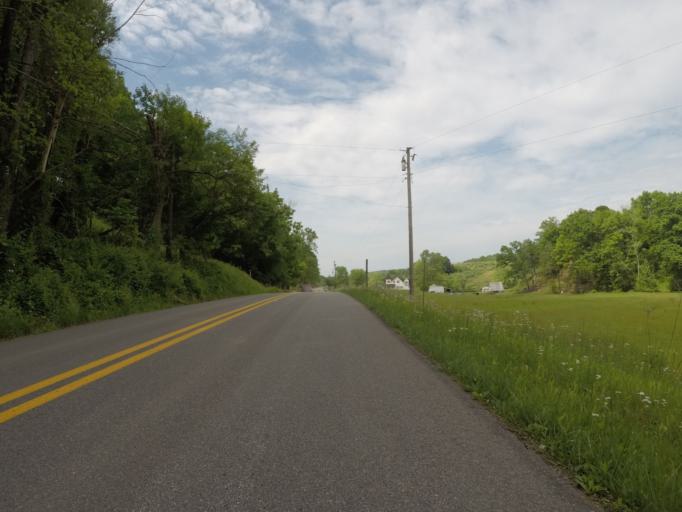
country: US
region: West Virginia
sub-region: Wayne County
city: Ceredo
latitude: 38.3474
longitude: -82.5649
